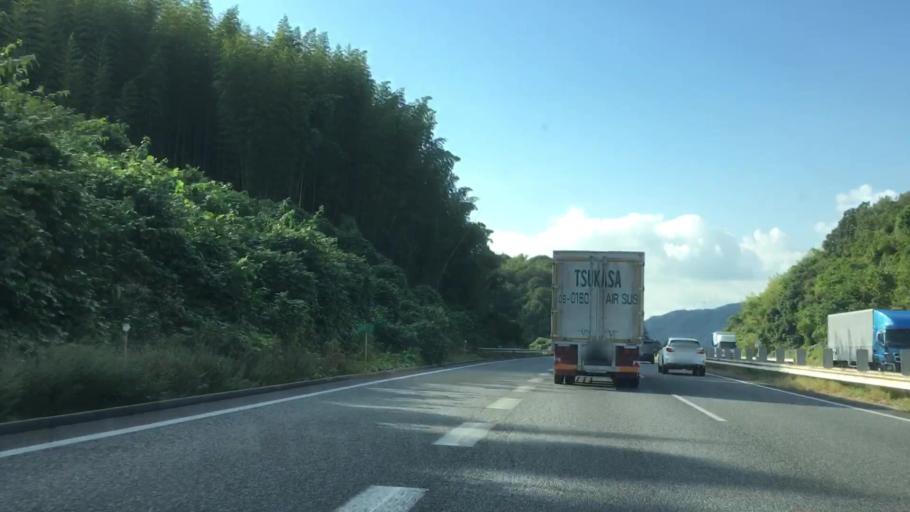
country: JP
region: Yamaguchi
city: Kudamatsu
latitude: 34.0327
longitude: 131.9327
